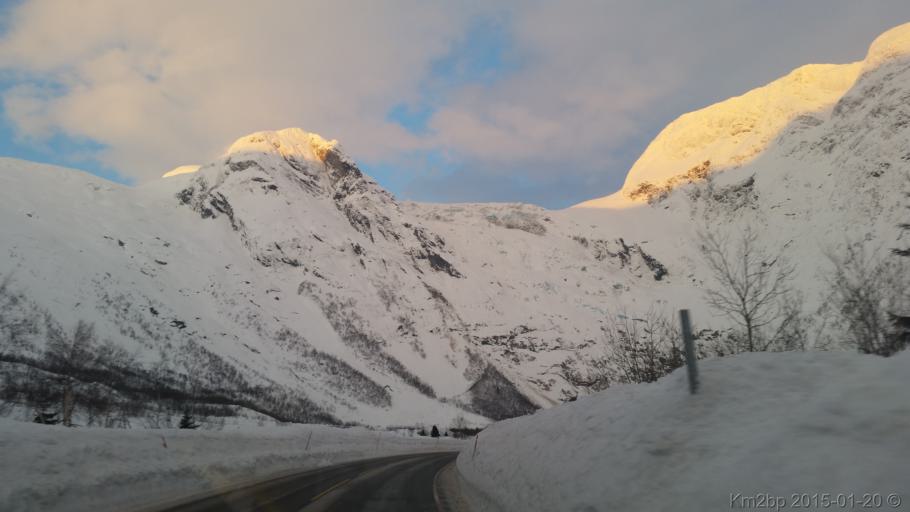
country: NO
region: Sogn og Fjordane
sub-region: Jolster
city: Skei
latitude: 61.4729
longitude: 6.7403
